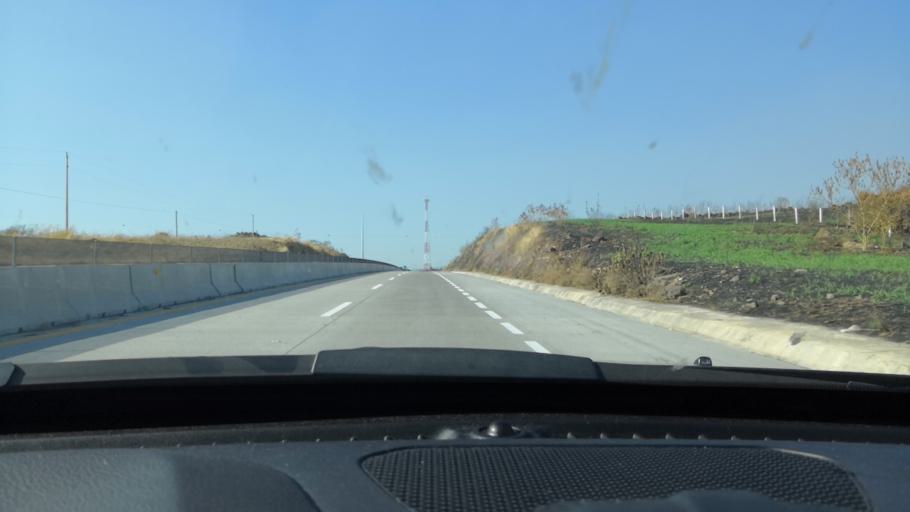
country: MX
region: Jalisco
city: Zapotlanejo
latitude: 20.6012
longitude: -103.1017
